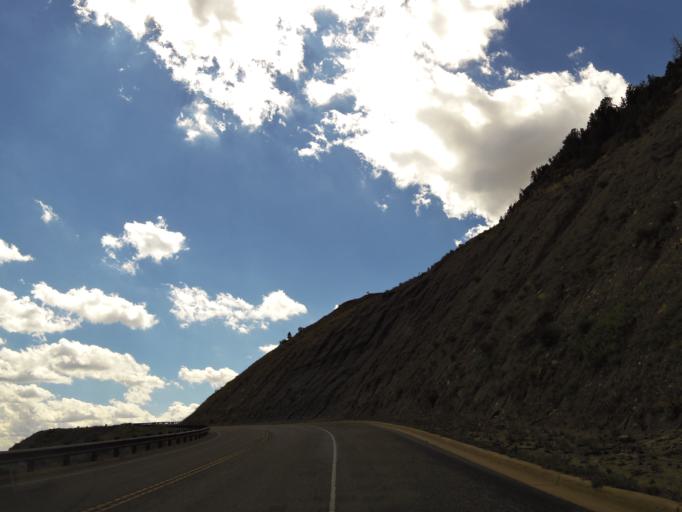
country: US
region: Colorado
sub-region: Montezuma County
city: Mancos
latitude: 37.3096
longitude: -108.4146
